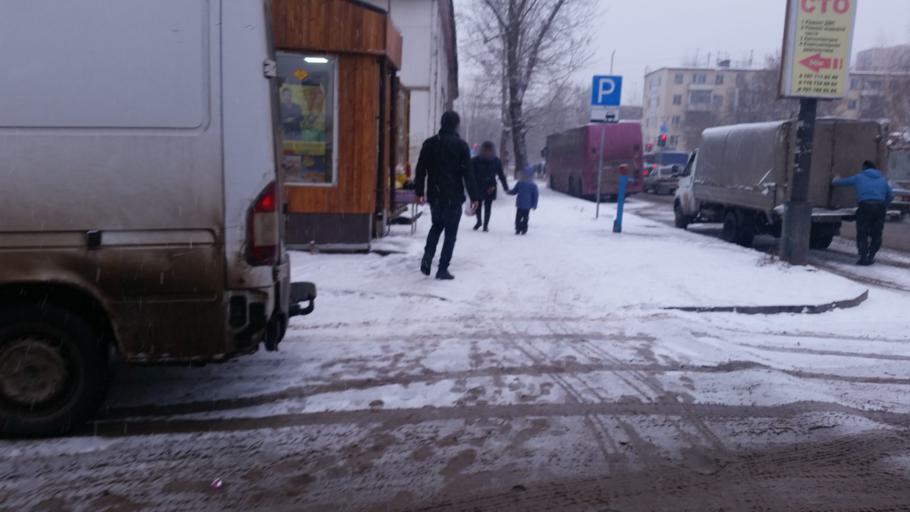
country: KZ
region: Astana Qalasy
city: Astana
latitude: 51.1631
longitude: 71.4648
